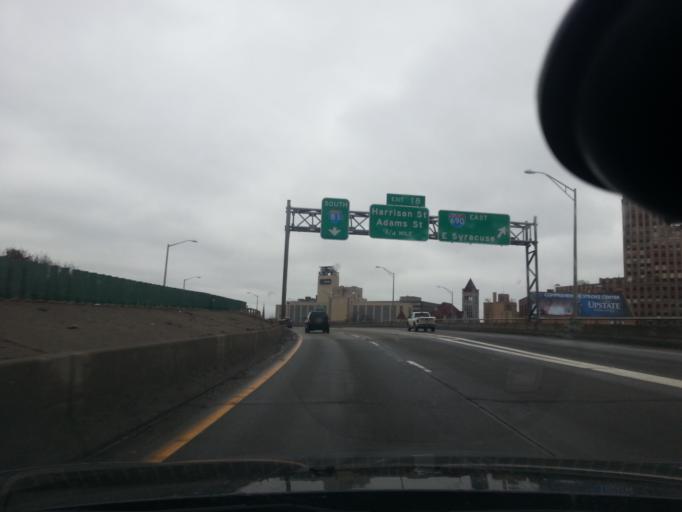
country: US
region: New York
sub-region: Onondaga County
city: Syracuse
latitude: 43.0528
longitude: -76.1509
